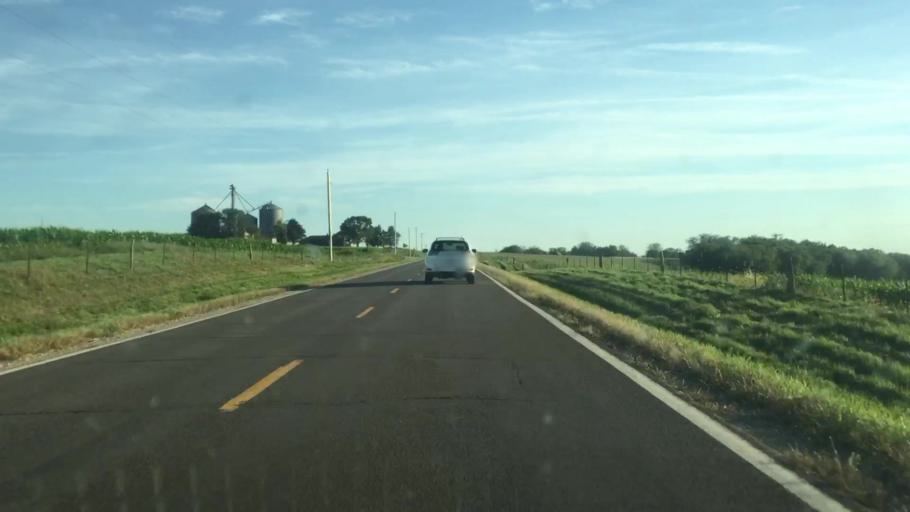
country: US
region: Kansas
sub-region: Brown County
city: Horton
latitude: 39.5784
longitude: -95.5270
